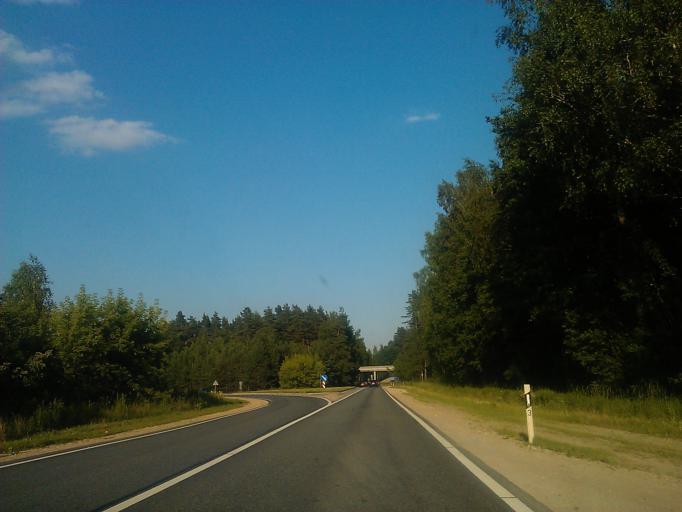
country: LV
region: Babite
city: Pinki
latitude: 56.9217
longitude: 23.9095
